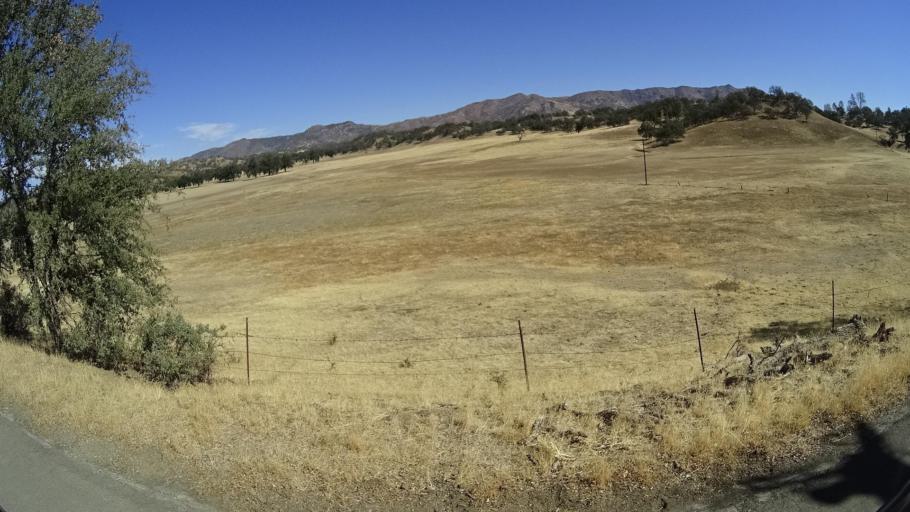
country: US
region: California
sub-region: Fresno County
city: Coalinga
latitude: 36.1760
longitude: -120.6946
